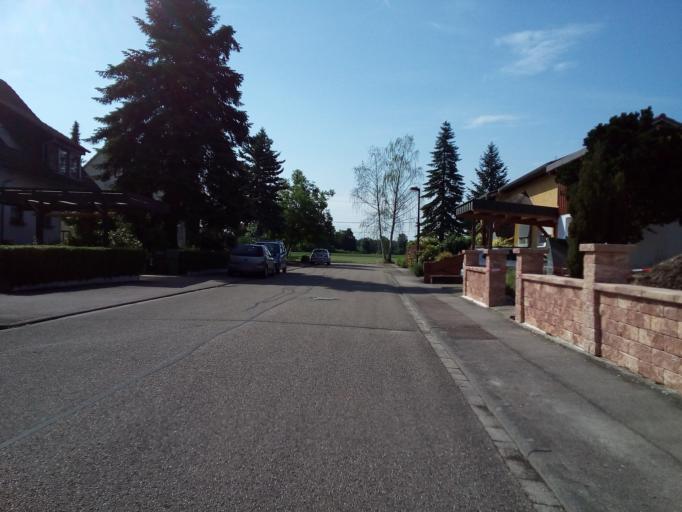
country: DE
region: Baden-Wuerttemberg
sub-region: Freiburg Region
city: Rheinau
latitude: 48.6438
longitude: 7.9296
